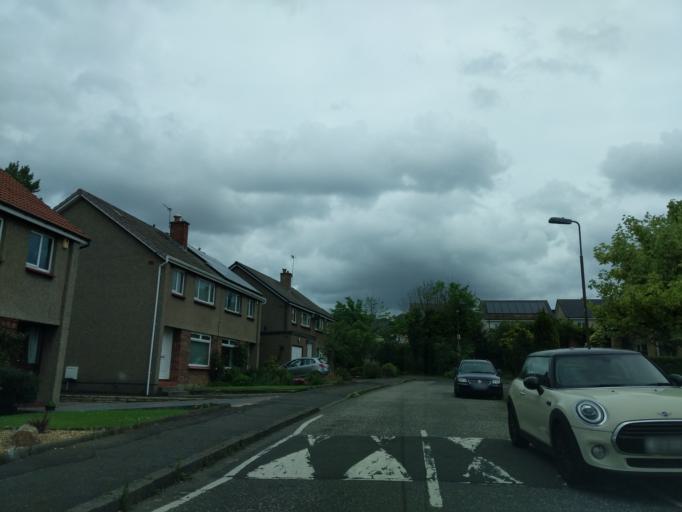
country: GB
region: Scotland
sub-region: Edinburgh
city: Colinton
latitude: 55.9513
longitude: -3.2880
